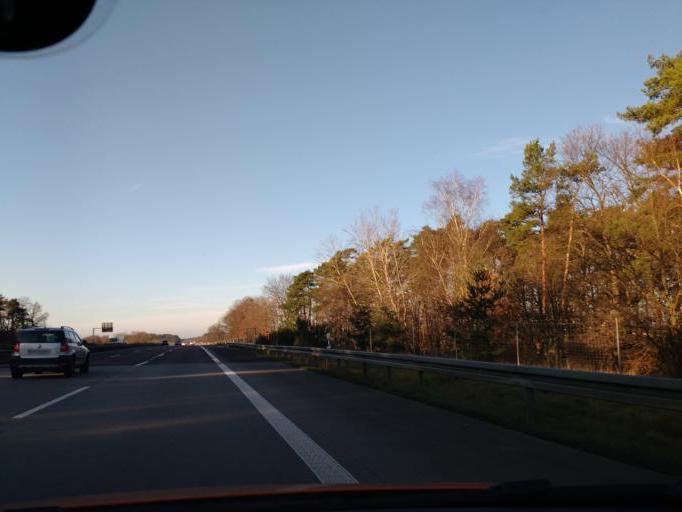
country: DE
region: Brandenburg
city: Ziesar
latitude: 52.2505
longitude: 12.2431
